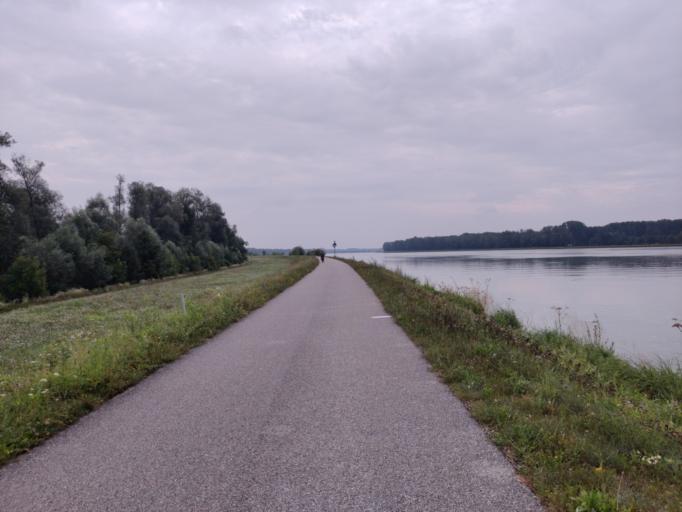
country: AT
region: Upper Austria
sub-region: Politischer Bezirk Urfahr-Umgebung
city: Steyregg
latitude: 48.2590
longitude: 14.4023
